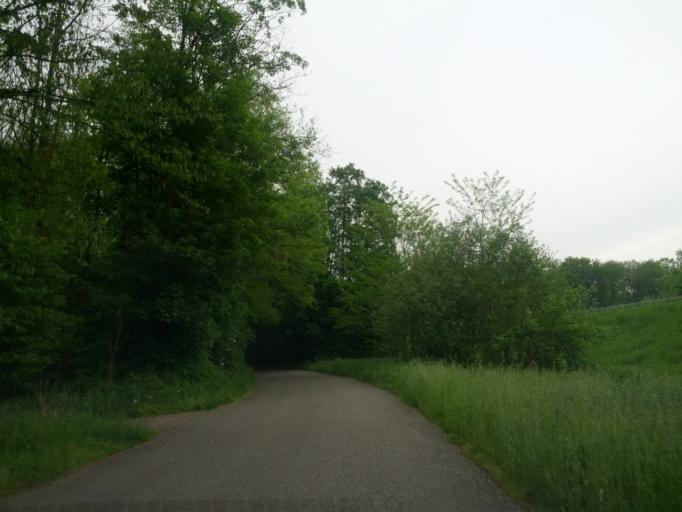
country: DE
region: Baden-Wuerttemberg
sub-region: Freiburg Region
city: Umkirch
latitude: 48.0255
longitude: 7.7842
